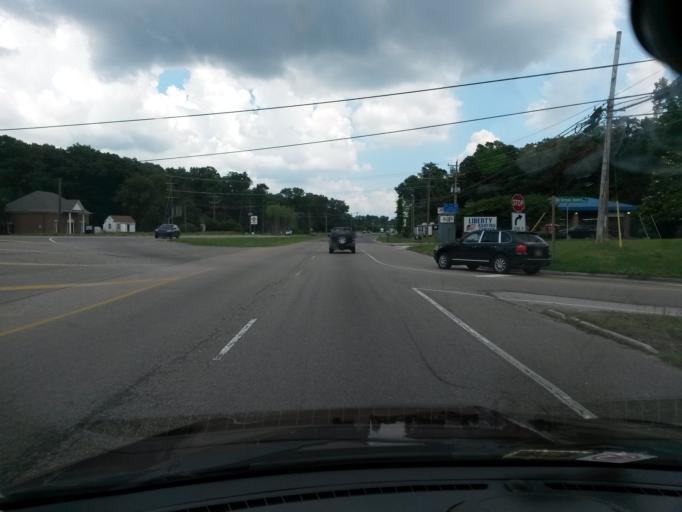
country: US
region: Virginia
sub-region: Chesterfield County
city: Enon
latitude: 37.3492
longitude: -77.3617
